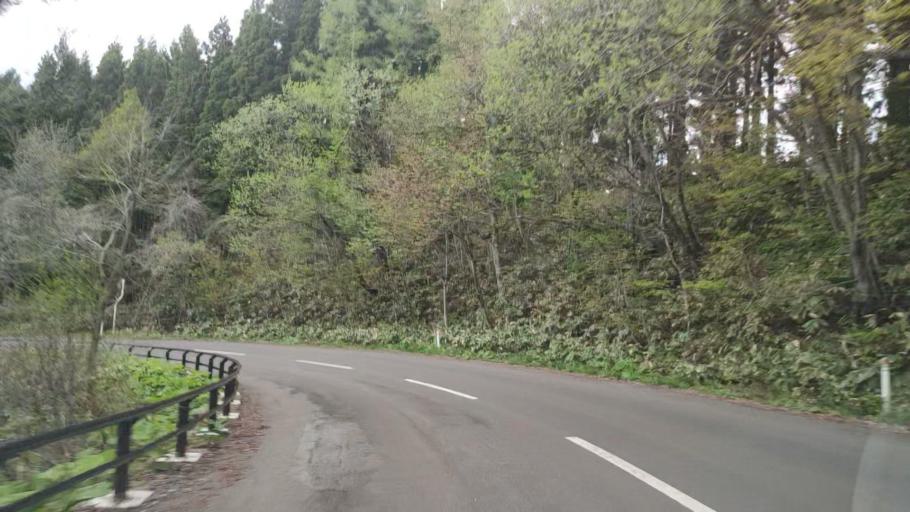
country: JP
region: Akita
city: Hanawa
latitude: 40.3745
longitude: 140.7899
